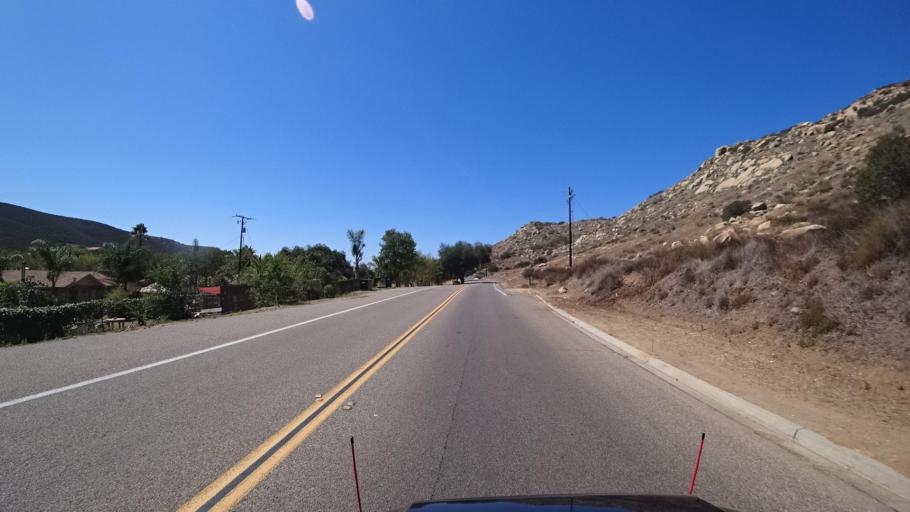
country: US
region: California
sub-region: San Diego County
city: San Diego Country Estates
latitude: 33.0016
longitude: -116.8323
